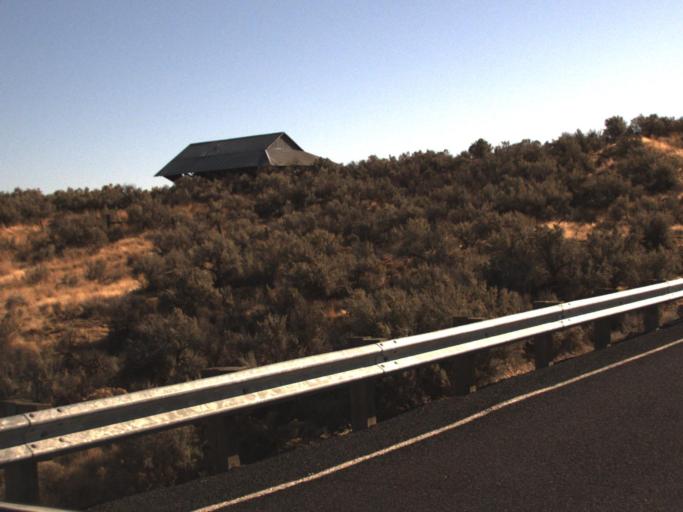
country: US
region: Washington
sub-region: Franklin County
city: Connell
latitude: 46.7719
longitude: -118.5476
